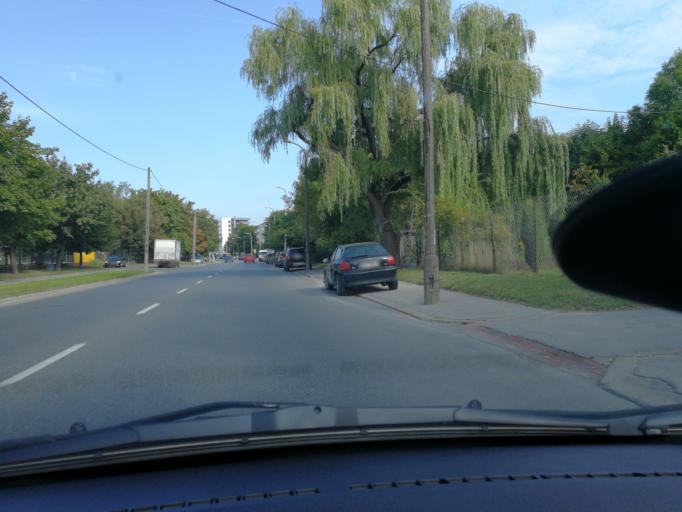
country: PL
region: Masovian Voivodeship
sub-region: Warszawa
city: Bemowo
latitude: 52.2315
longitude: 20.9418
